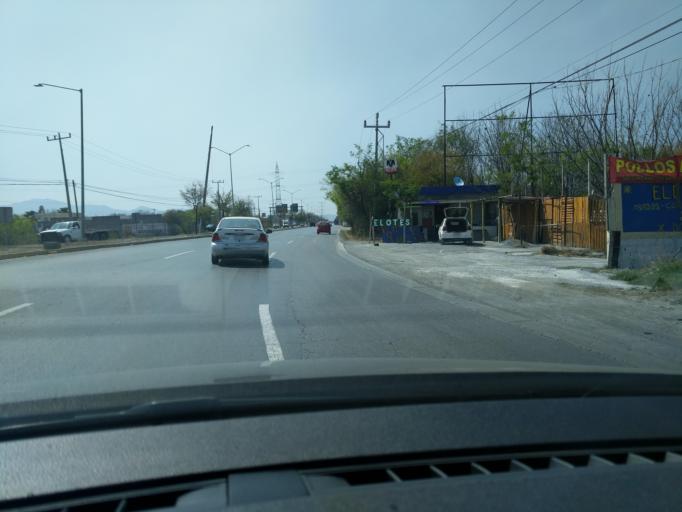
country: MX
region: Nuevo Leon
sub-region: Garcia
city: Valle de Lincoln
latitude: 25.7898
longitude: -100.4976
